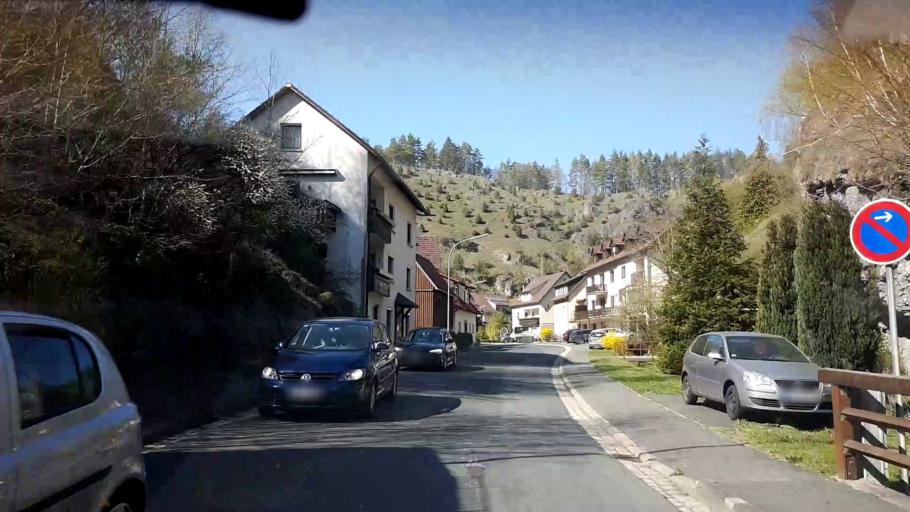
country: DE
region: Bavaria
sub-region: Upper Franconia
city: Pottenstein
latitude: 49.7731
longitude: 11.4127
